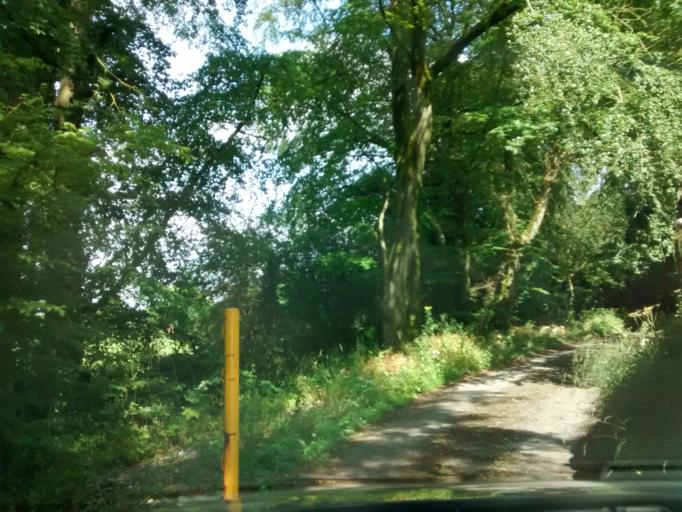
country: IE
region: Leinster
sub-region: Uibh Fhaili
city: Clara
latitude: 53.3700
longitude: -7.6248
